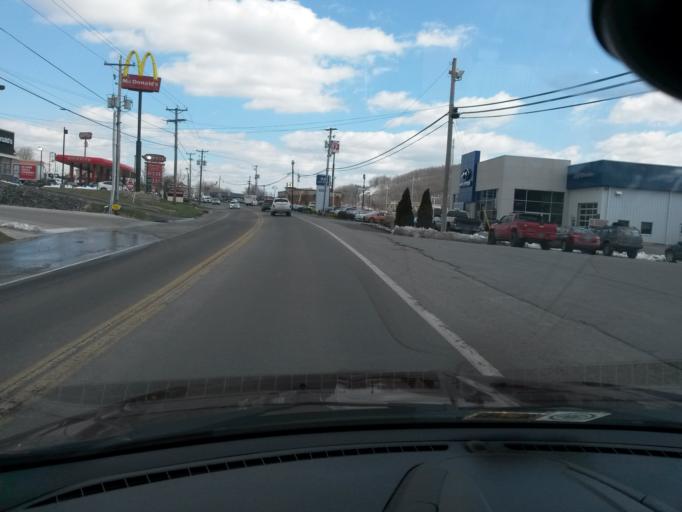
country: US
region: West Virginia
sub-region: Mercer County
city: Princeton
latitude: 37.3627
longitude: -81.0594
